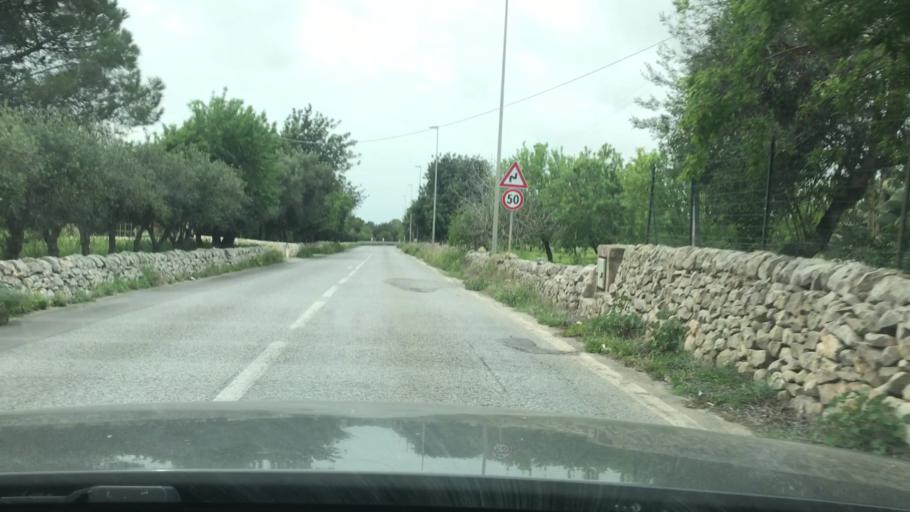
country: IT
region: Sicily
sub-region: Ragusa
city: Scicli
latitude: 36.8017
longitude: 14.7175
